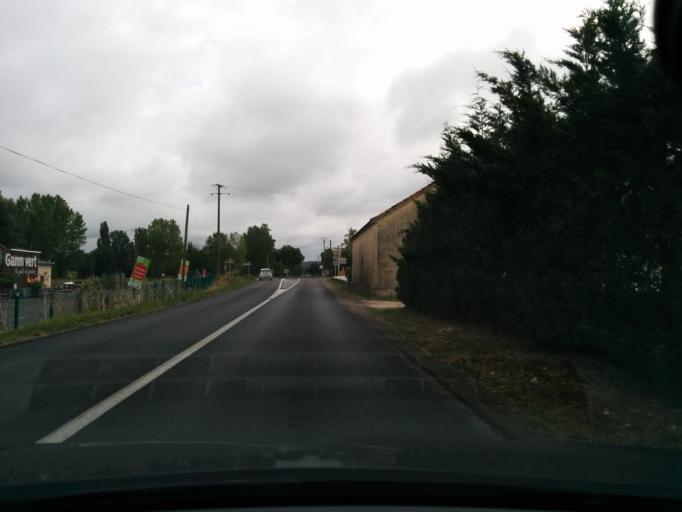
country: FR
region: Midi-Pyrenees
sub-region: Departement du Lot
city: Montcuq
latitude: 44.3432
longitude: 1.2081
